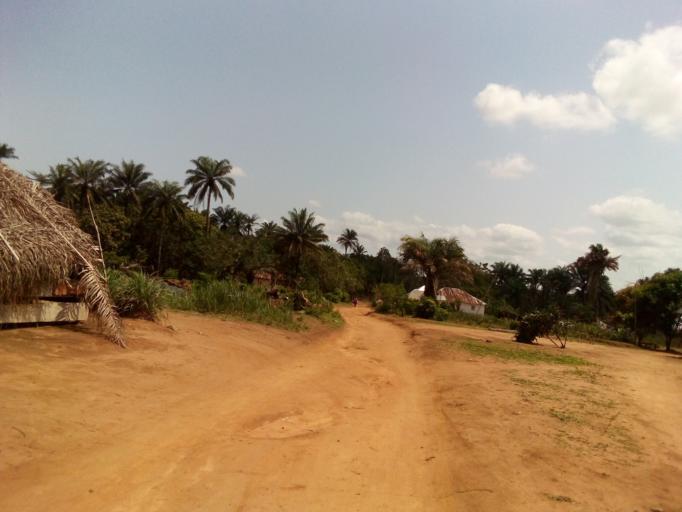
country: SL
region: Western Area
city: Waterloo
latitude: 8.3528
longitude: -13.0181
